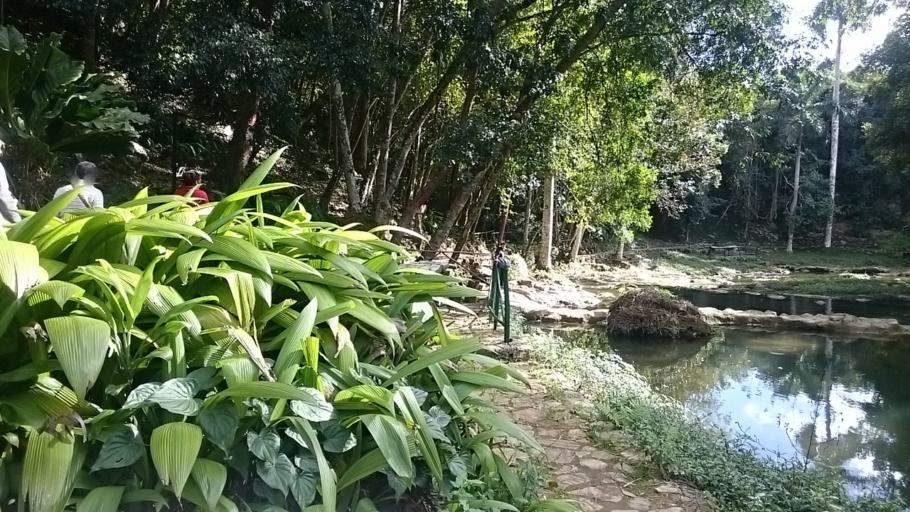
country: CU
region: Artemisa
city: Soroa
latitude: 22.8246
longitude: -82.9256
